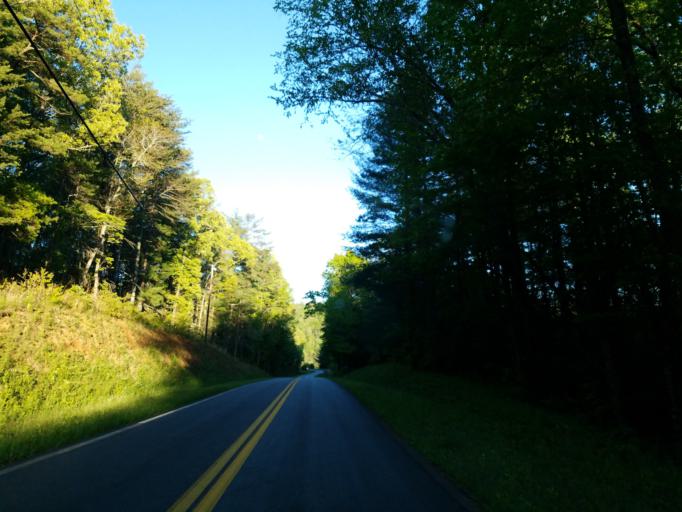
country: US
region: Georgia
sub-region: Union County
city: Blairsville
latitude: 34.7393
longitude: -84.0672
